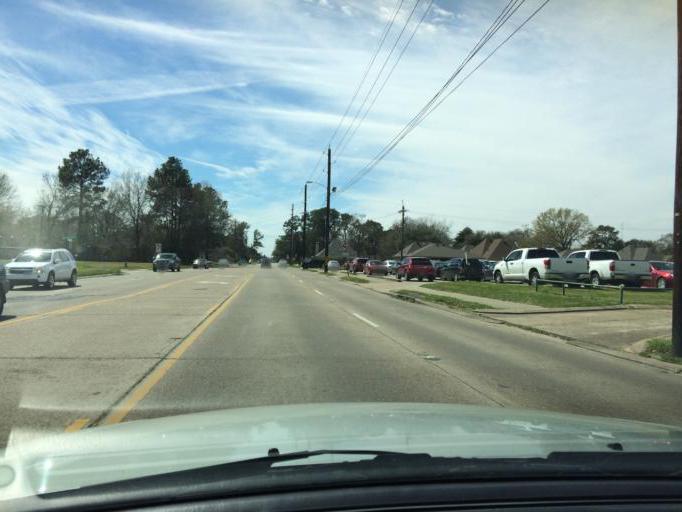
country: US
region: Louisiana
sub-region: Lafayette Parish
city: Lafayette
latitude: 30.2065
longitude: -92.0578
